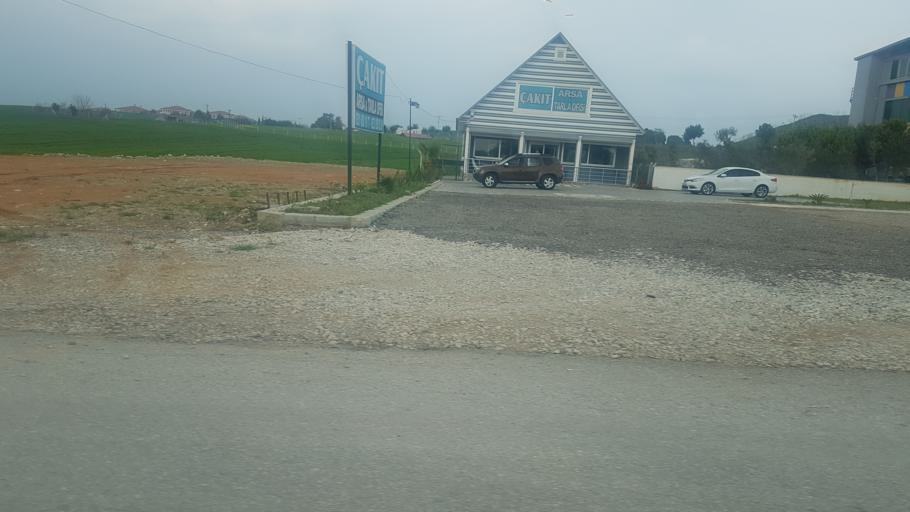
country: TR
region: Adana
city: Seyhan
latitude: 37.0578
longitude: 35.2429
